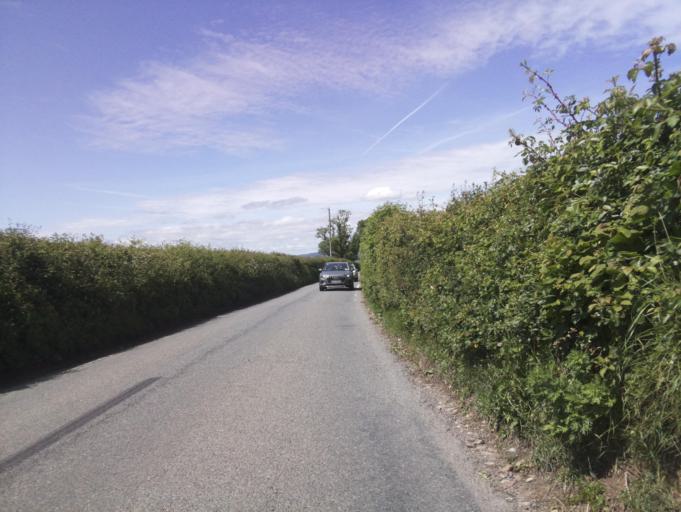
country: GB
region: England
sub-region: Devon
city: Ottery St Mary
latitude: 50.8207
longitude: -3.2719
